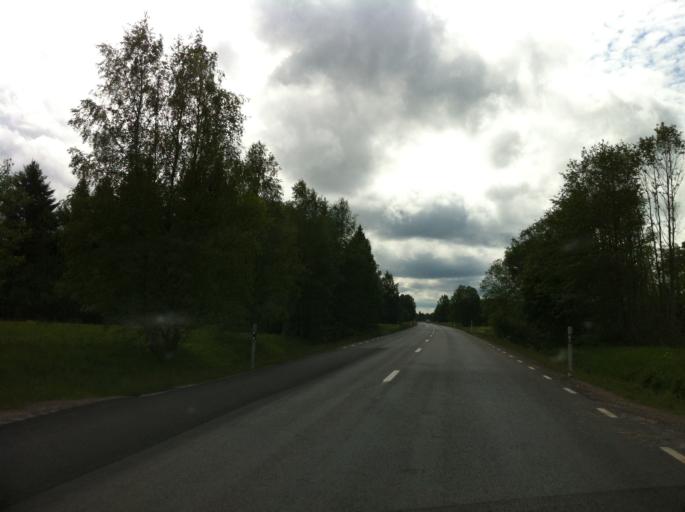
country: SE
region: Vaermland
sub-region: Sunne Kommun
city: Sunne
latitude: 59.7163
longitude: 13.1395
